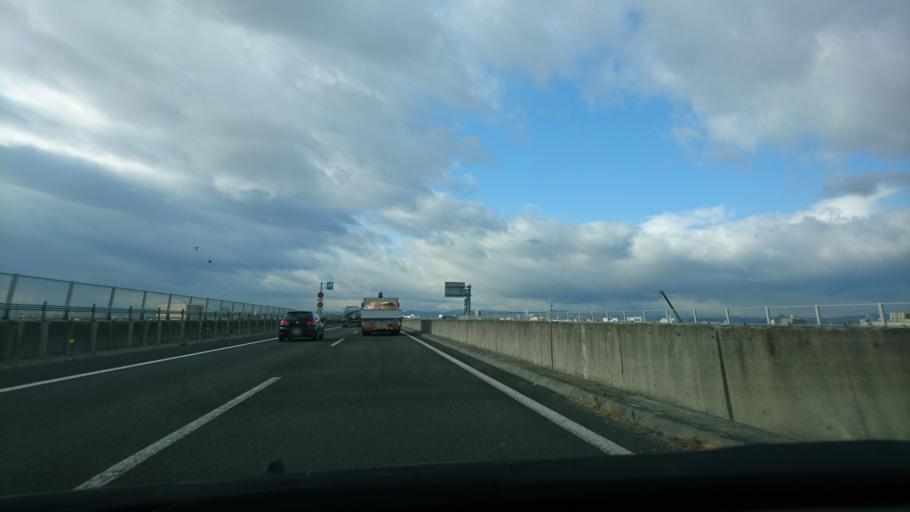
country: JP
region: Miyagi
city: Rifu
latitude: 38.2644
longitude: 140.9720
